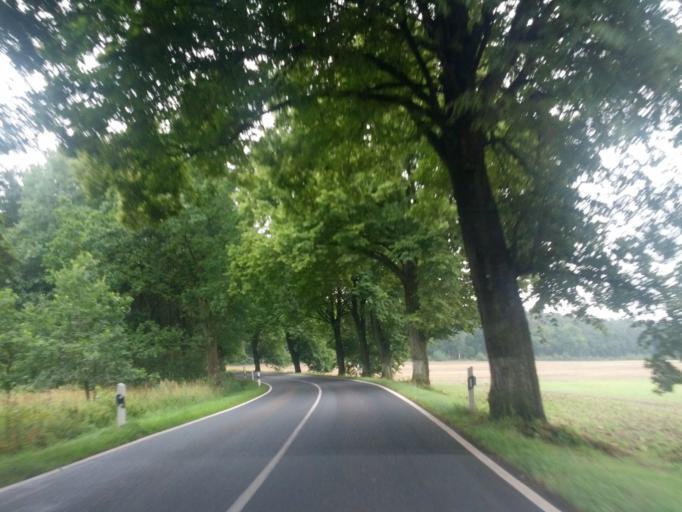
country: DE
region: Mecklenburg-Vorpommern
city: Biendorf
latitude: 54.0686
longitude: 11.6700
